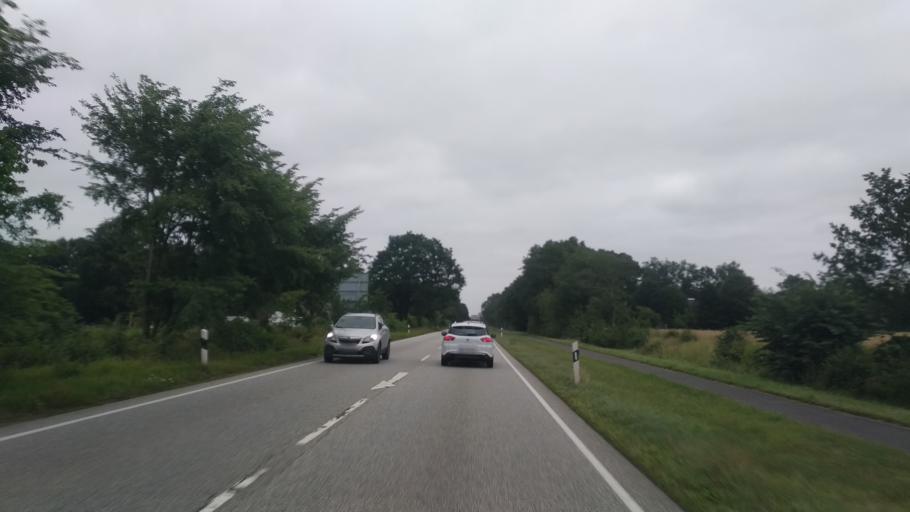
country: DE
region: Schleswig-Holstein
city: Oeversee
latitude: 54.6956
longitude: 9.4330
